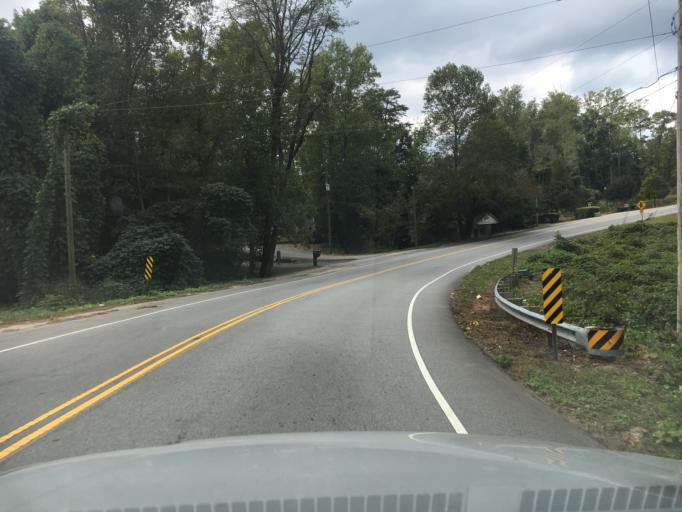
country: US
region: South Carolina
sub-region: Greenville County
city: Greer
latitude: 34.9551
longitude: -82.2303
